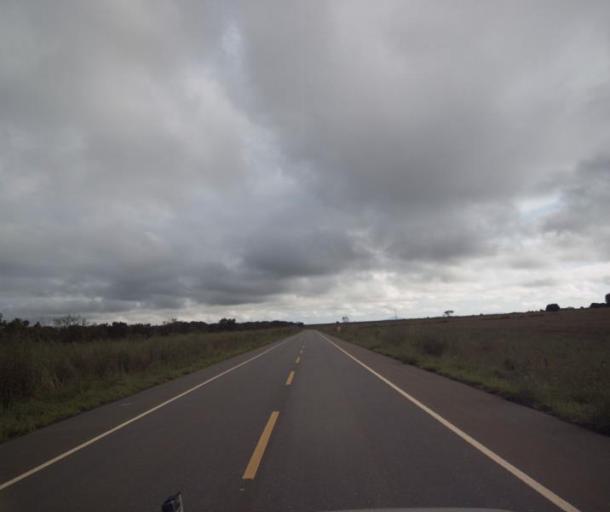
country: BR
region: Goias
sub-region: Padre Bernardo
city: Padre Bernardo
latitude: -15.3405
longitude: -48.6475
